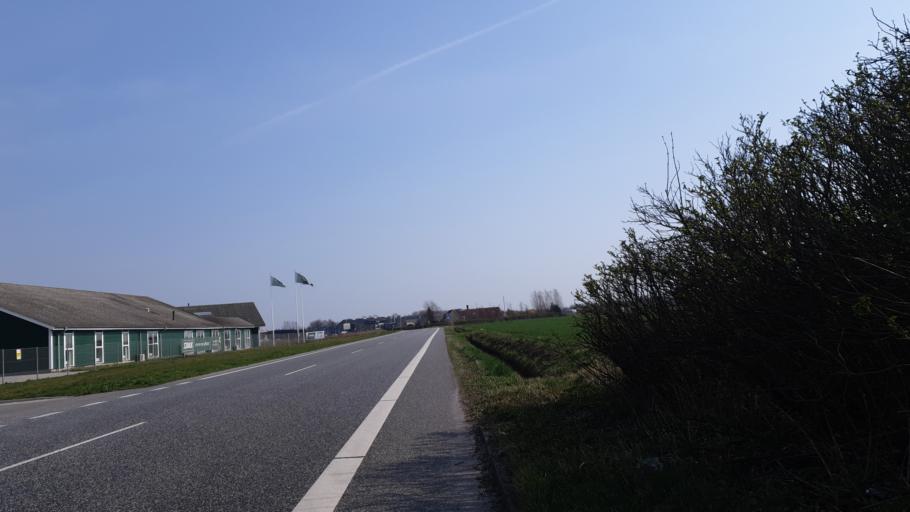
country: DK
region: Central Jutland
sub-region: Hedensted Kommune
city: Hedensted
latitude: 55.7837
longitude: 9.6847
